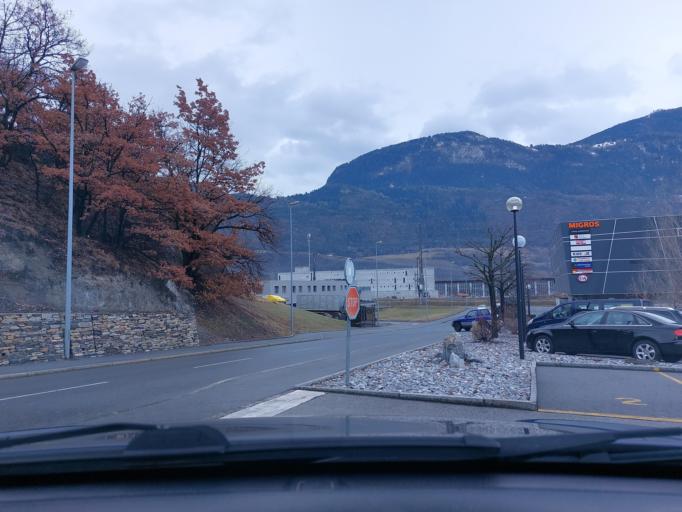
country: CH
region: Valais
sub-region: Sierre District
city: Chalais
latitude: 46.2826
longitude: 7.5137
